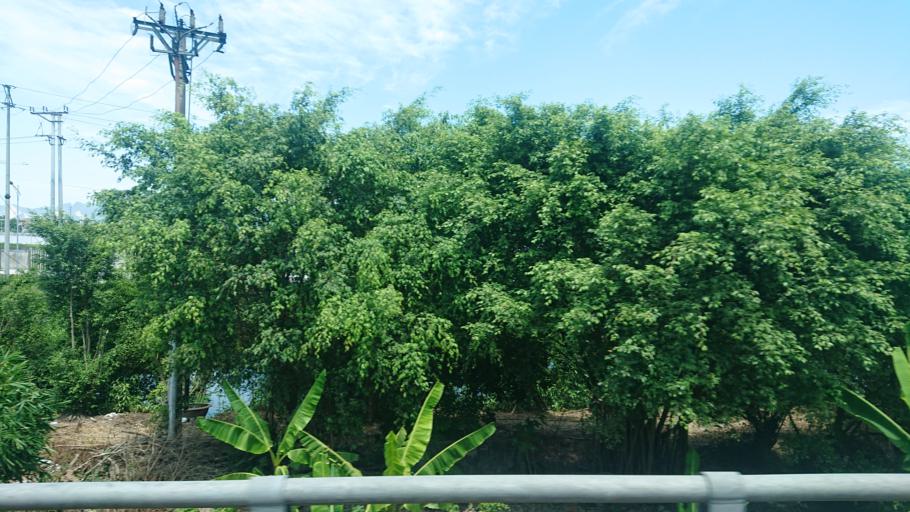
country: VN
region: Ha Nam
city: Thanh Pho Phu Ly
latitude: 20.5409
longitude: 105.9475
